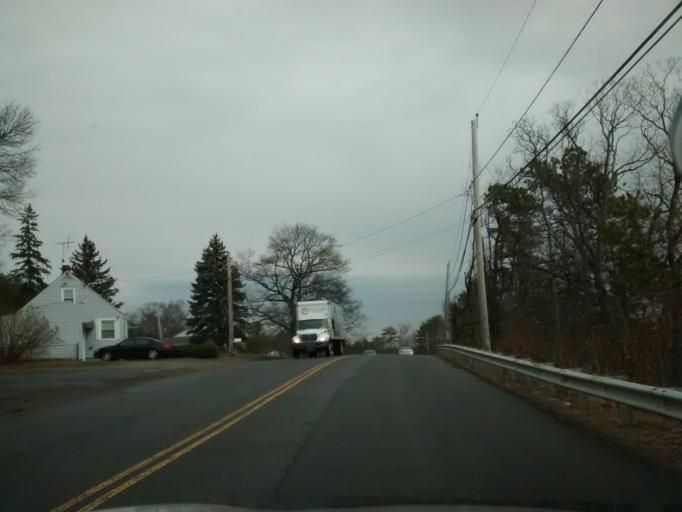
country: US
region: Massachusetts
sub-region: Worcester County
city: Hamilton
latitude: 42.2819
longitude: -71.7577
